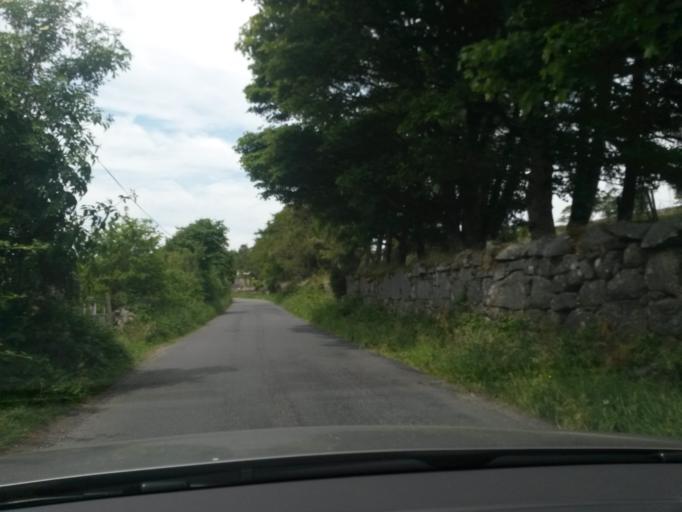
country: IE
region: Leinster
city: Ballinteer
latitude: 53.1963
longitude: -6.2840
